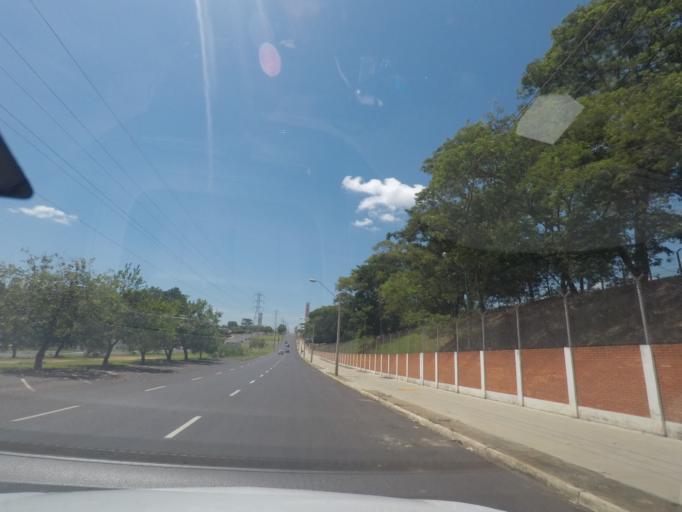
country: BR
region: Sao Paulo
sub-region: Matao
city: Matao
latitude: -21.6117
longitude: -48.3755
